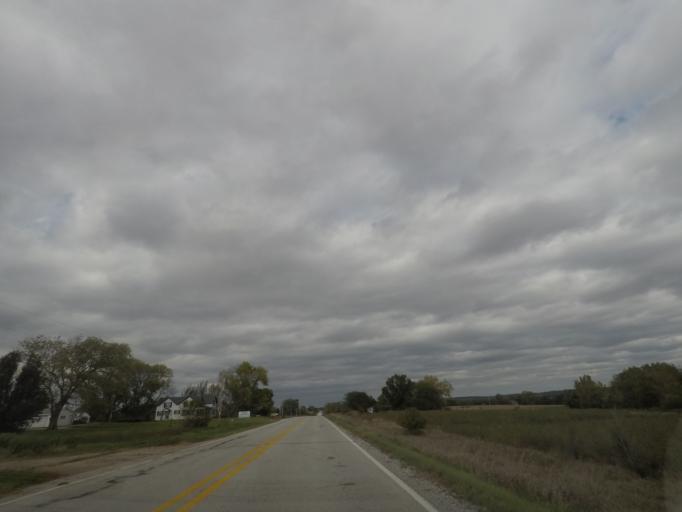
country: US
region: Iowa
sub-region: Story County
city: Huxley
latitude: 41.8611
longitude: -93.5316
